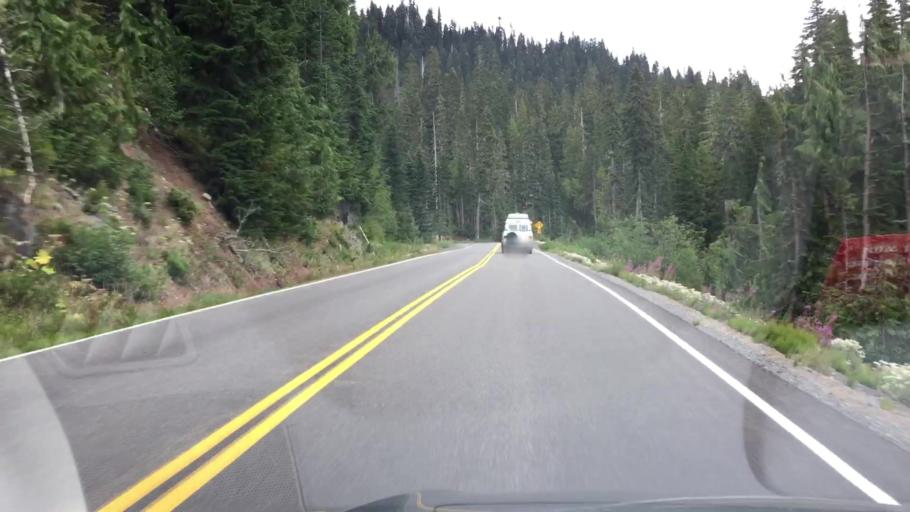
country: US
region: Washington
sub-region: Pierce County
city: Buckley
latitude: 46.7775
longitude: -121.7446
